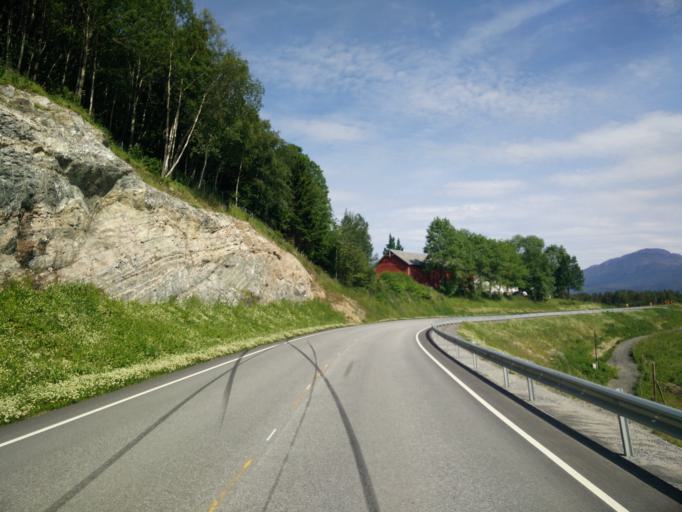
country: NO
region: More og Romsdal
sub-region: Tingvoll
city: Tingvoll
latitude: 63.0510
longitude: 8.0979
